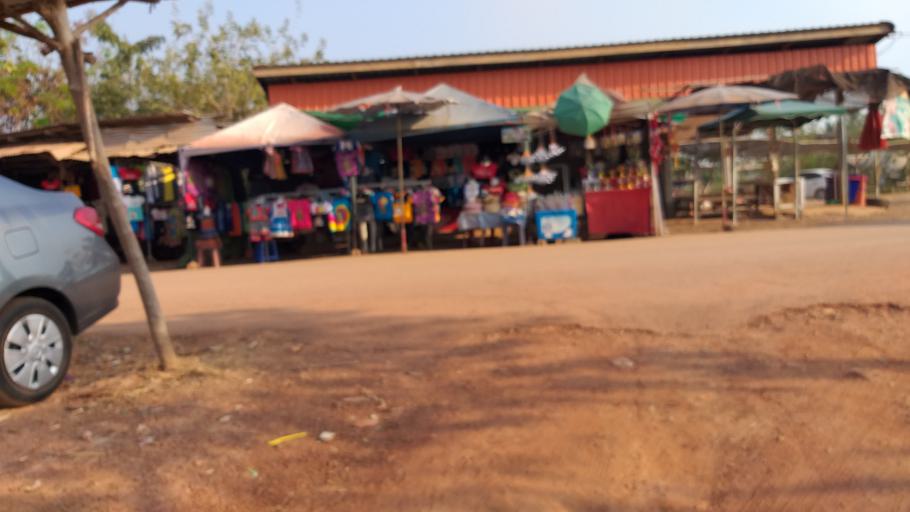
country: TH
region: Changwat Udon Thani
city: Ban Dung
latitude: 17.7425
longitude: 103.3576
